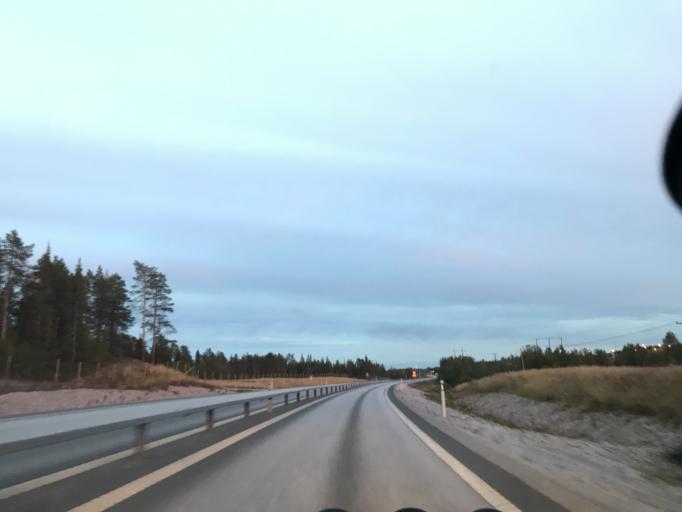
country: SE
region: Norrbotten
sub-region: Gallivare Kommun
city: Malmberget
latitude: 67.6579
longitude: 21.0067
